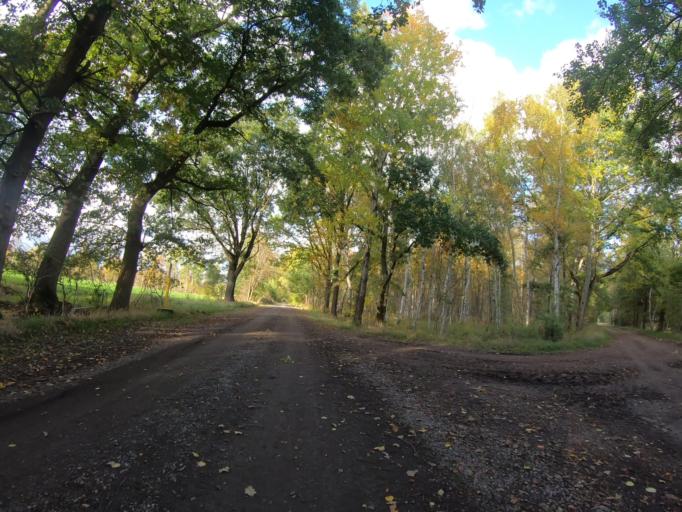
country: DE
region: Lower Saxony
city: Wagenhoff
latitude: 52.5523
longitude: 10.5576
